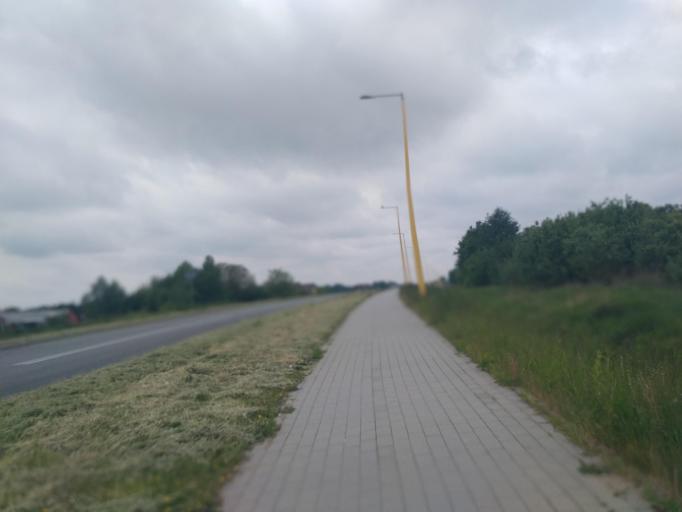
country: PL
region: Subcarpathian Voivodeship
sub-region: Krosno
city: Krosno
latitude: 49.6719
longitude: 21.7500
